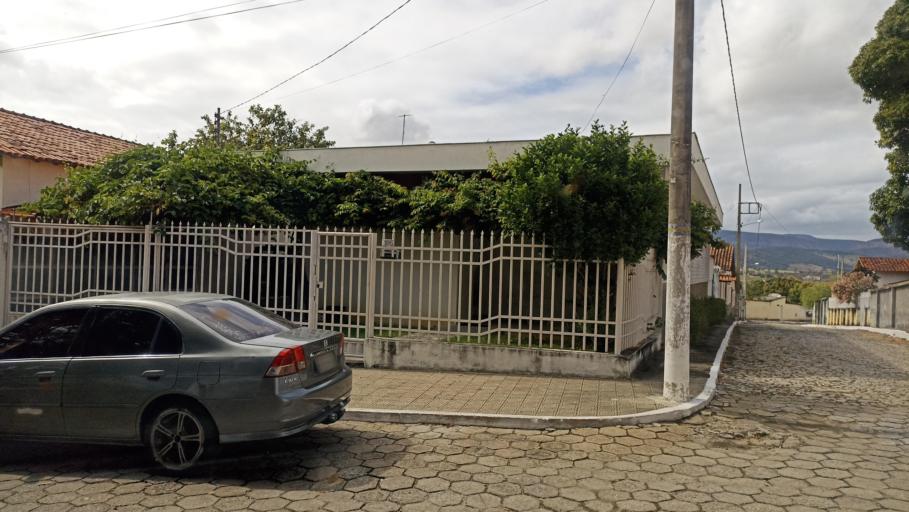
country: BR
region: Minas Gerais
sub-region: Jequitinhonha
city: Jequitinhonha
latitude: -16.4341
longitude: -41.0035
